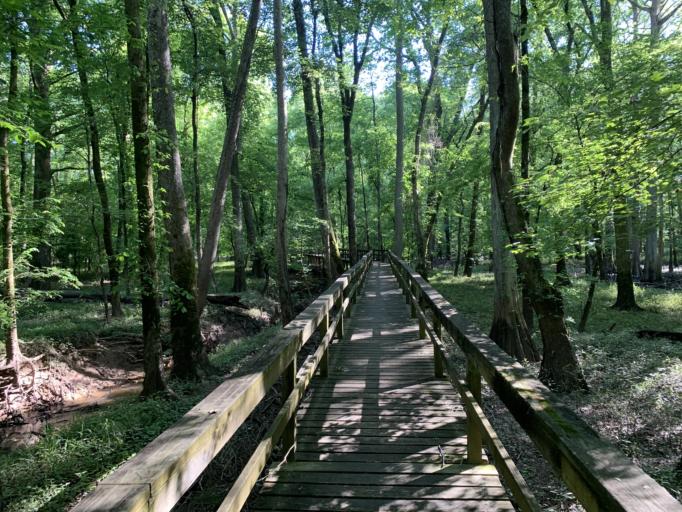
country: US
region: Tennessee
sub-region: Chester County
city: Henderson
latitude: 35.4902
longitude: -88.6812
